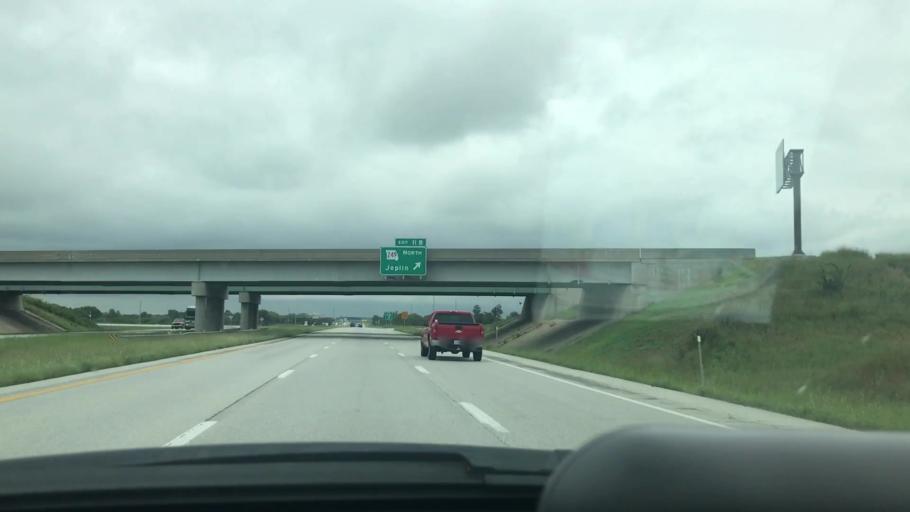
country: US
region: Missouri
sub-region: Jasper County
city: Duenweg
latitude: 37.0610
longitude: -94.4279
